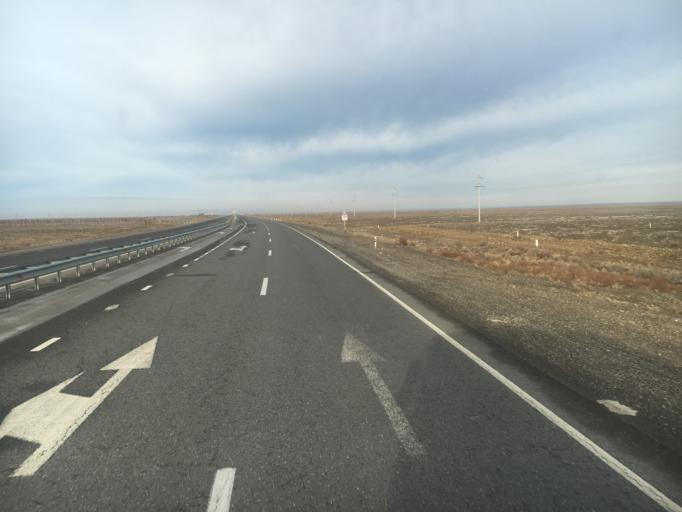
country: KZ
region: Ongtustik Qazaqstan
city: Turkestan
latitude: 43.5016
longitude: 67.8437
